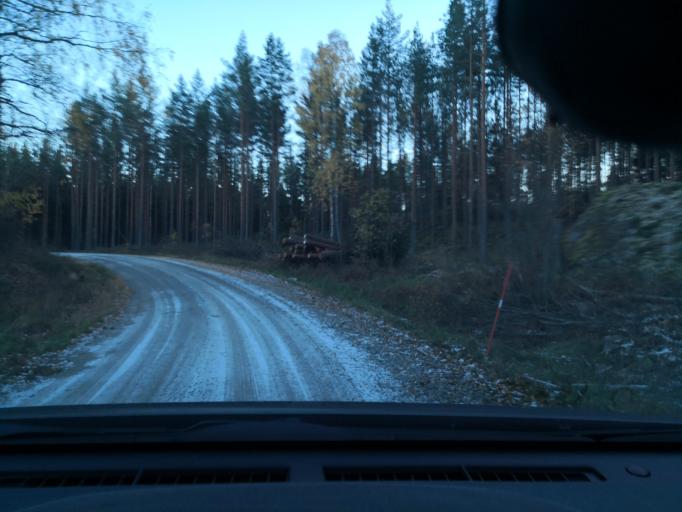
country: SE
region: Vaestmanland
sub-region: Vasteras
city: Tillberga
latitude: 59.7645
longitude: 16.6118
